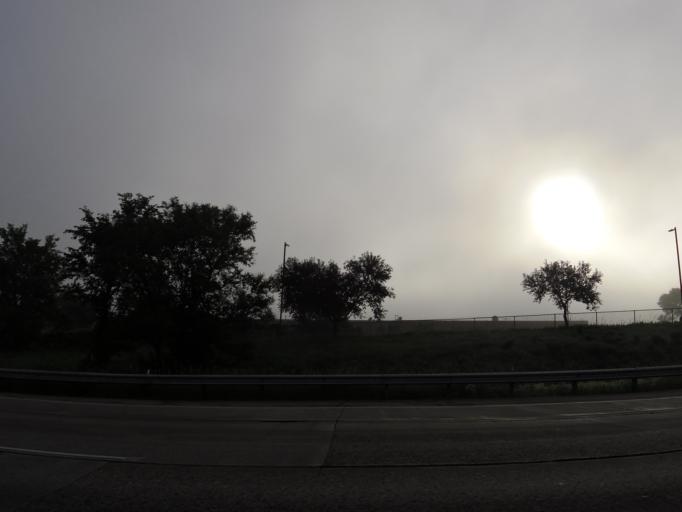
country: US
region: Minnesota
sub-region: Hennepin County
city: Maple Grove
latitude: 45.1018
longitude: -93.4564
